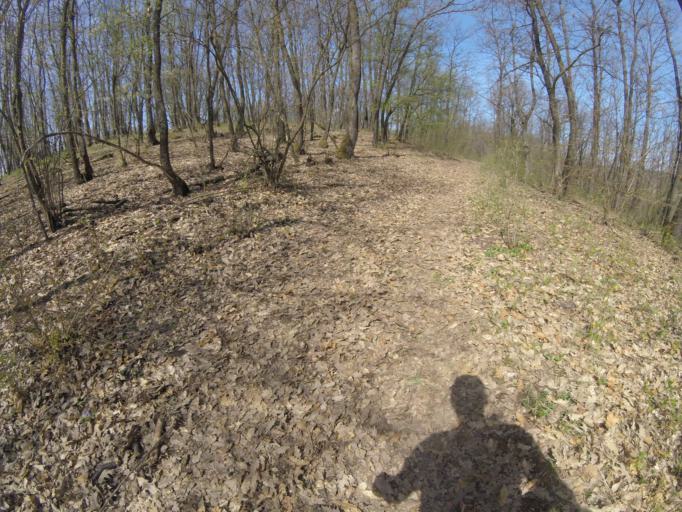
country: HU
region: Borsod-Abauj-Zemplen
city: Szendro
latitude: 48.4233
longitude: 20.7546
